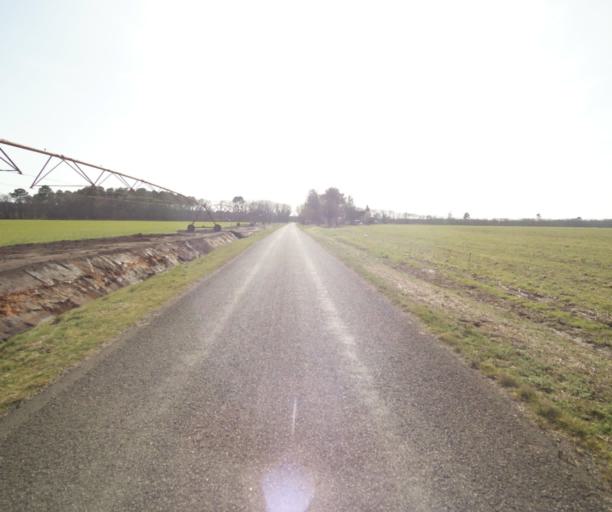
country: FR
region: Aquitaine
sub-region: Departement des Landes
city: Roquefort
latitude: 44.1495
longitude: -0.1728
